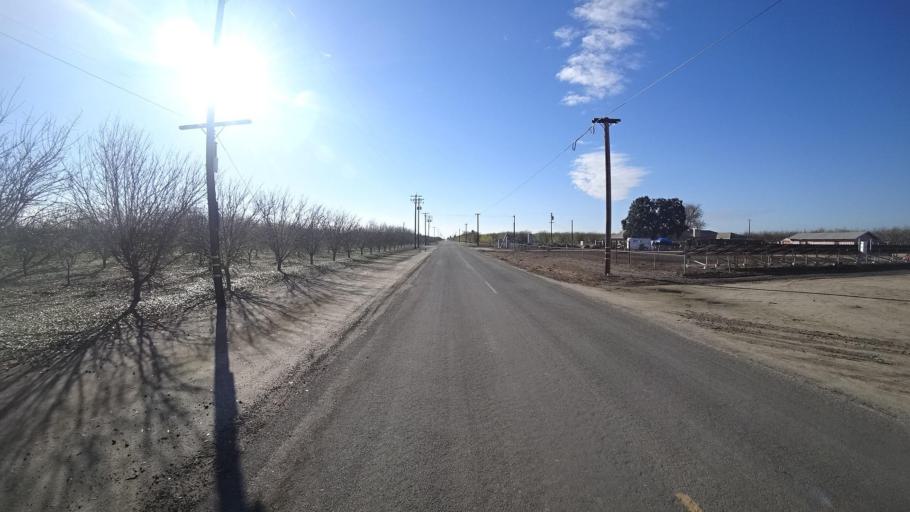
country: US
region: California
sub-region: Kern County
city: Delano
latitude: 35.7332
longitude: -119.3118
